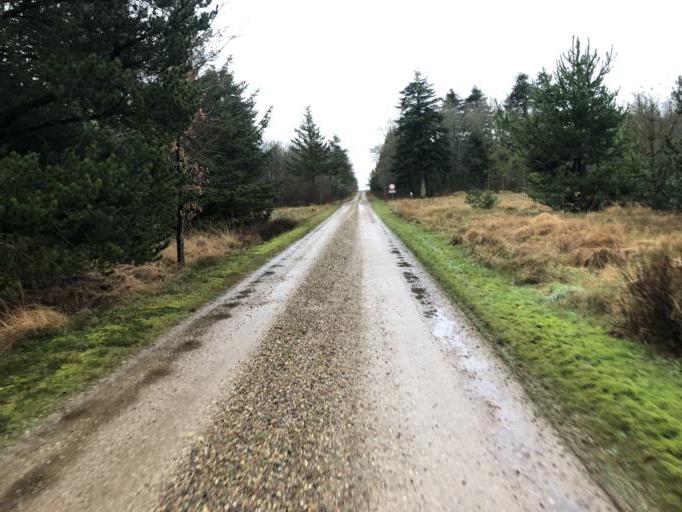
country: DK
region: Central Jutland
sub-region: Holstebro Kommune
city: Ulfborg
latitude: 56.2909
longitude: 8.4561
